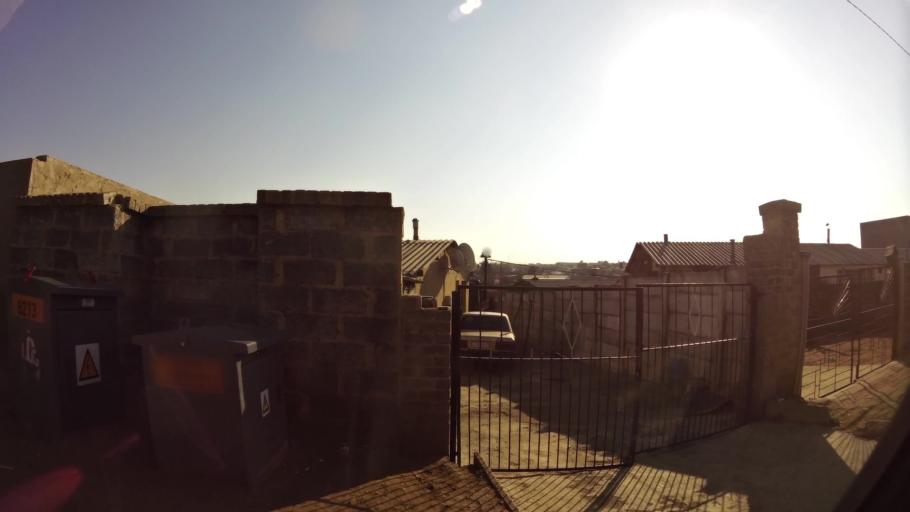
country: ZA
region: Gauteng
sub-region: City of Johannesburg Metropolitan Municipality
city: Soweto
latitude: -26.2566
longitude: 27.9449
